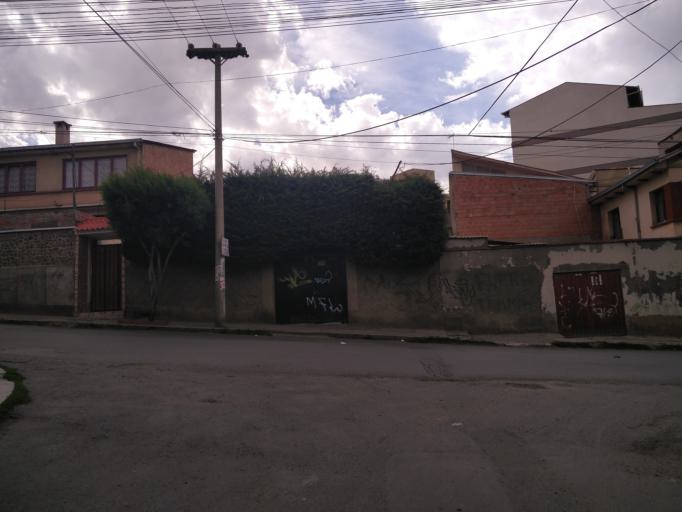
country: BO
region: La Paz
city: La Paz
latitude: -16.5176
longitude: -68.1281
